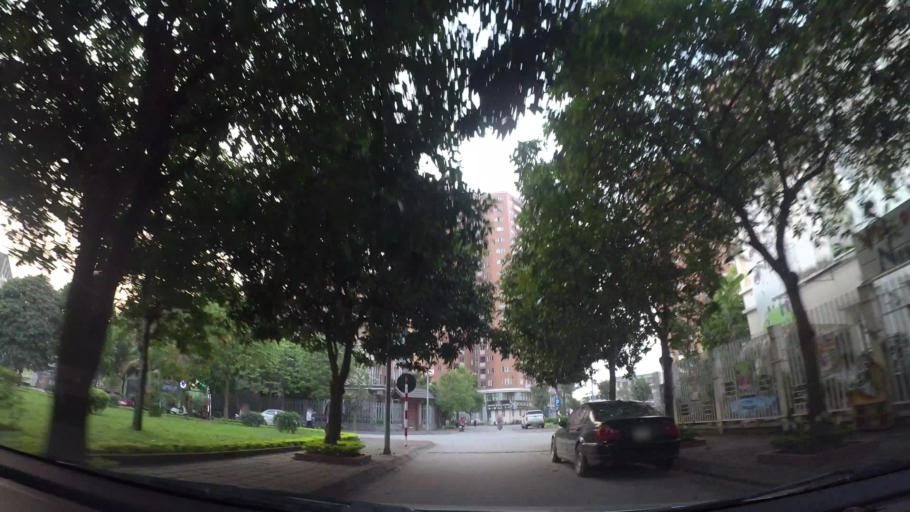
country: VN
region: Ha Noi
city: Cau Giay
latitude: 21.0504
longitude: 105.7937
